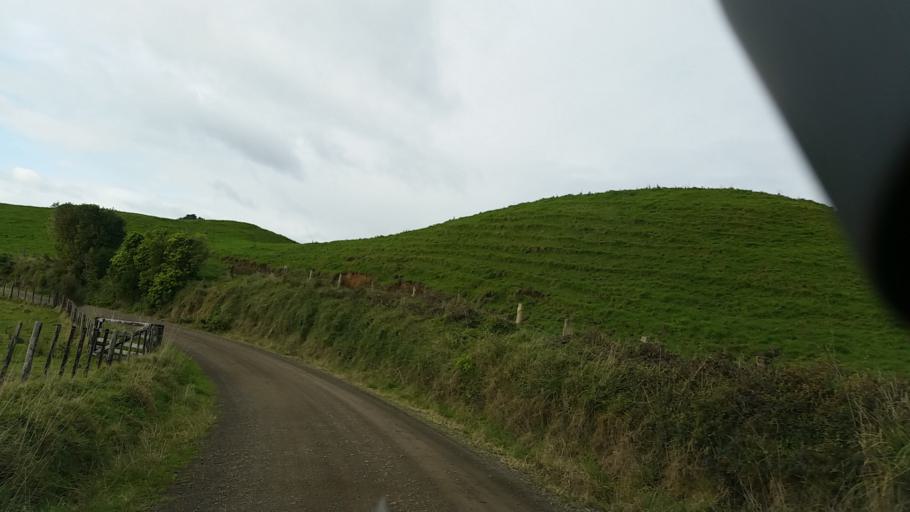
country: NZ
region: Taranaki
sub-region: New Plymouth District
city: Waitara
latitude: -39.0633
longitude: 174.3804
